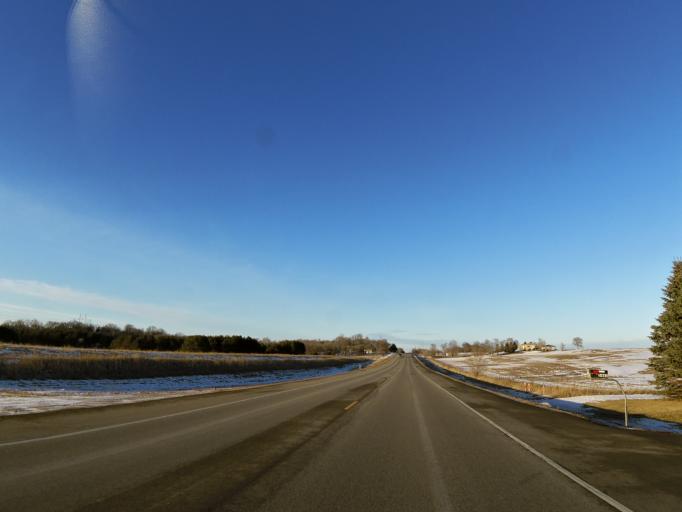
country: US
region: Minnesota
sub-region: Washington County
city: Cottage Grove
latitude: 44.8693
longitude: -92.9033
